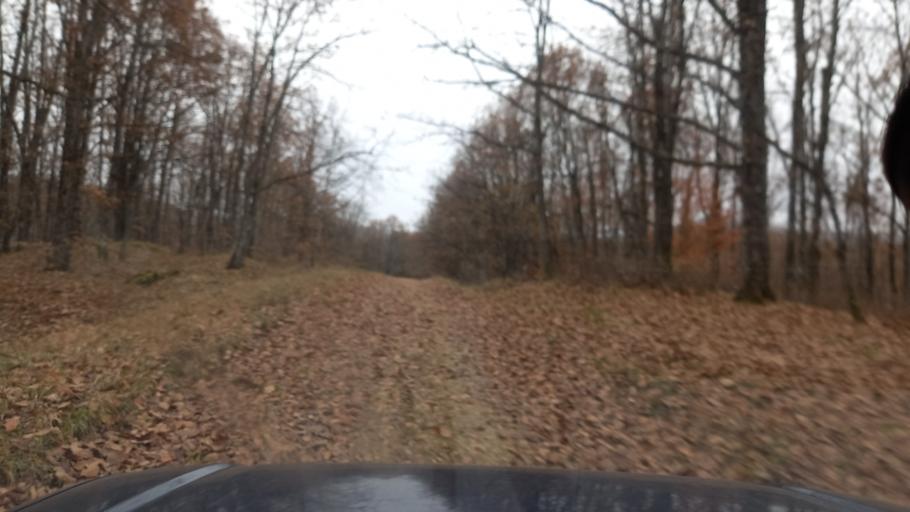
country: RU
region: Krasnodarskiy
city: Goryachiy Klyuch
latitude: 44.5020
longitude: 39.2830
